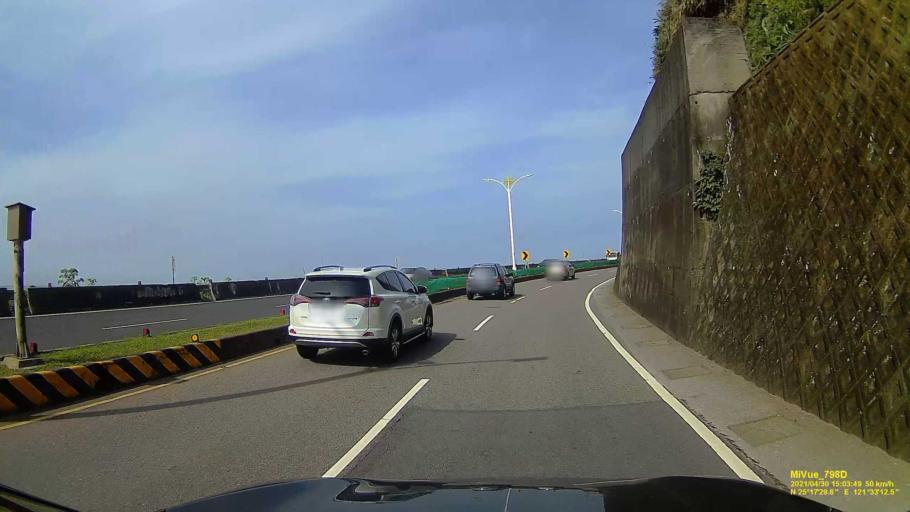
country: TW
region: Taipei
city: Taipei
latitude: 25.2917
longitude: 121.5537
